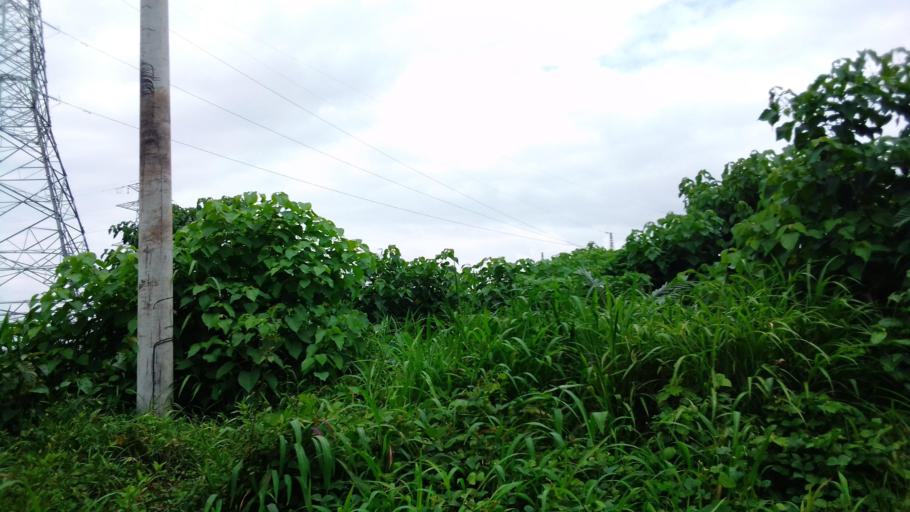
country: SL
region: Eastern Province
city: Kenema
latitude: 7.8210
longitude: -11.1802
